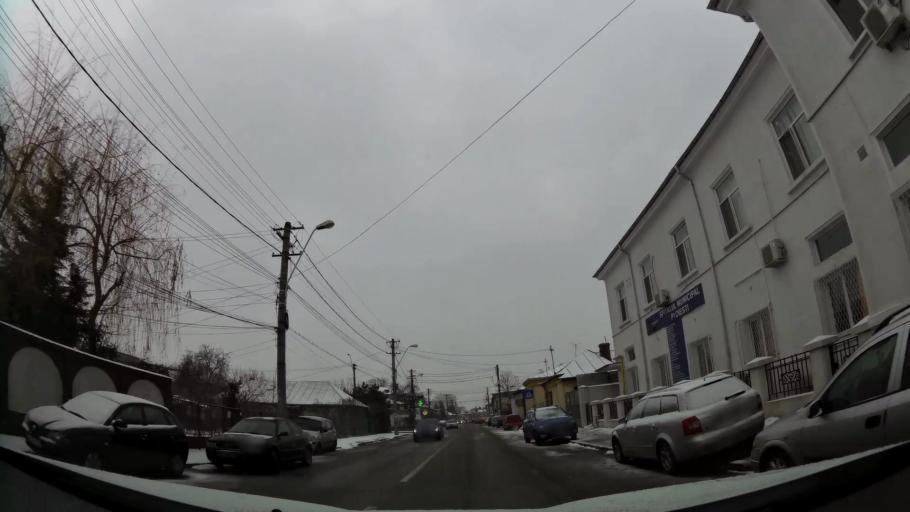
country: RO
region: Prahova
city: Ploiesti
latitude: 44.9316
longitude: 26.0195
